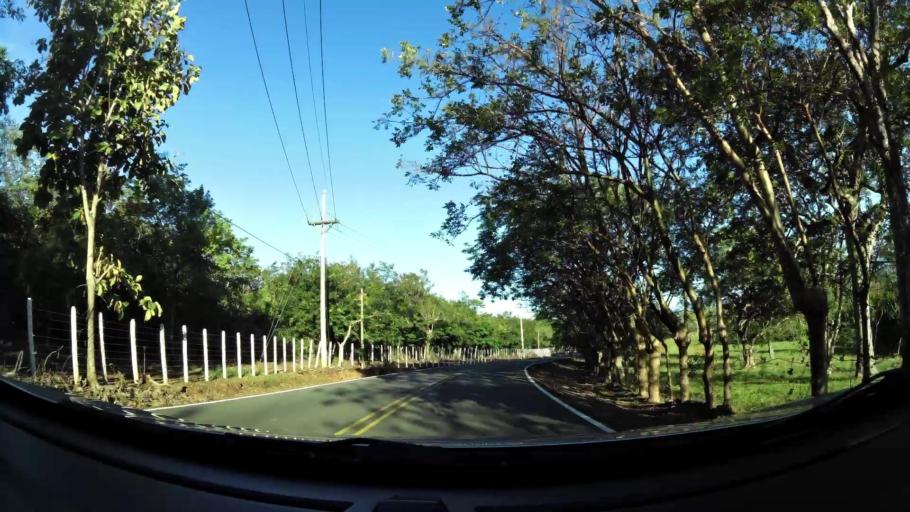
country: CR
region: Puntarenas
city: Miramar
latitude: 10.1092
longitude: -84.8268
